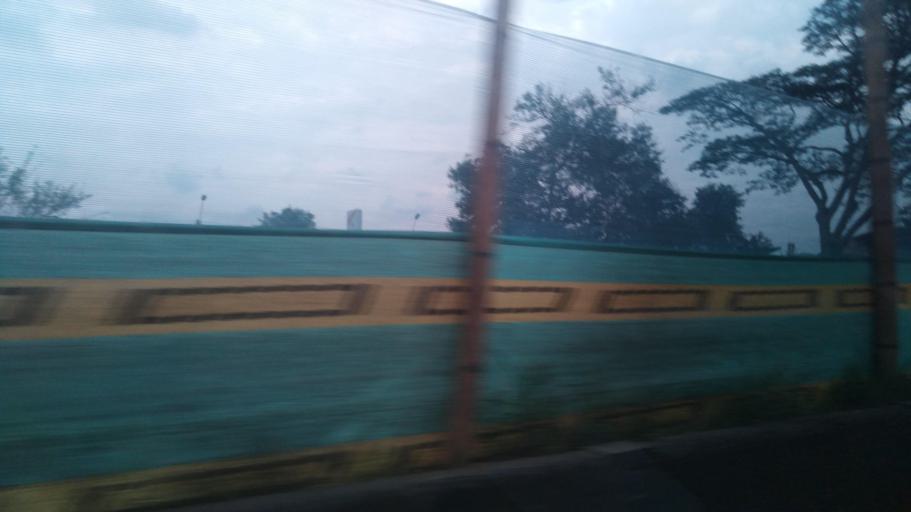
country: CO
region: Valle del Cauca
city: Cali
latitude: 3.4181
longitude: -76.5090
